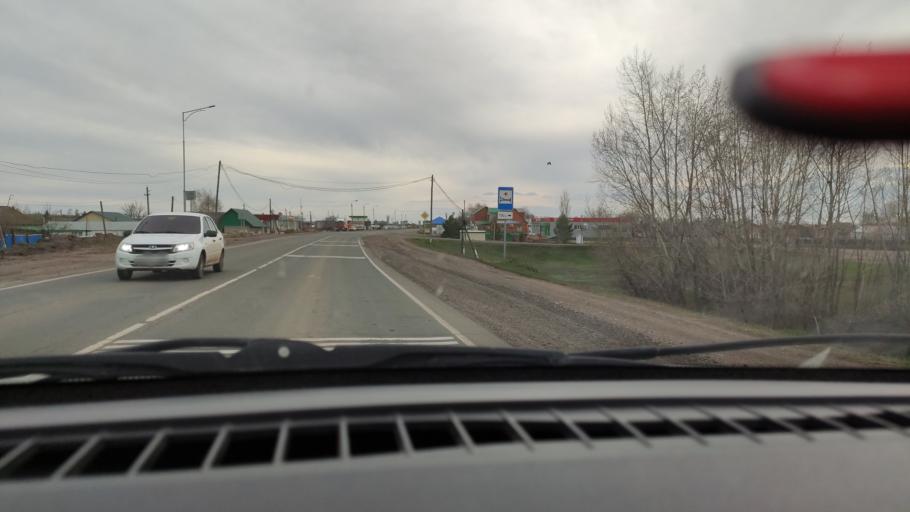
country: RU
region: Bashkortostan
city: Mayachnyy
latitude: 52.4273
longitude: 55.7867
